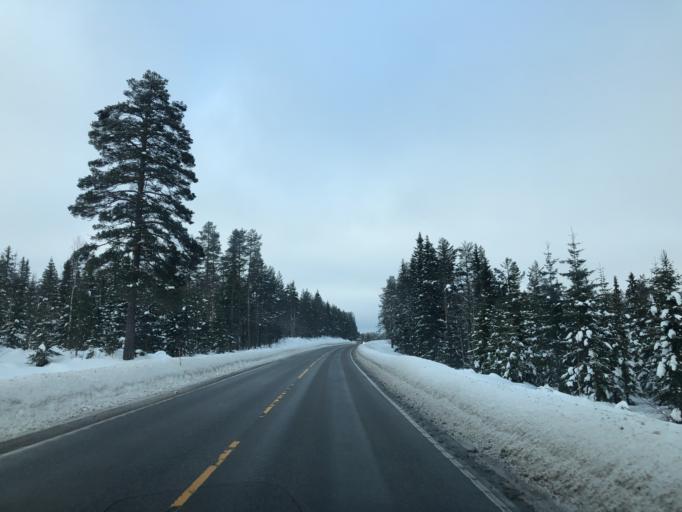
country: NO
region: Hedmark
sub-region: Trysil
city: Innbygda
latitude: 61.2247
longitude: 12.2462
